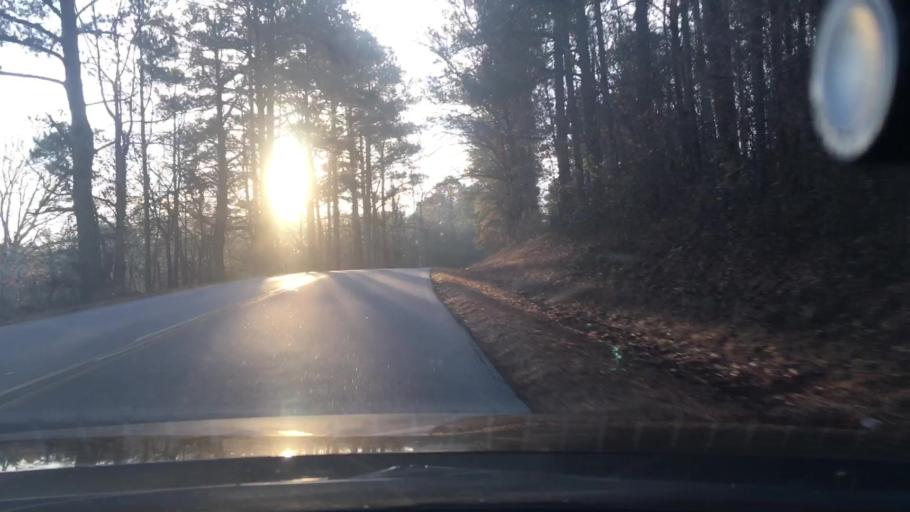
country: US
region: Georgia
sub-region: Coweta County
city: Senoia
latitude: 33.3174
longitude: -84.4803
